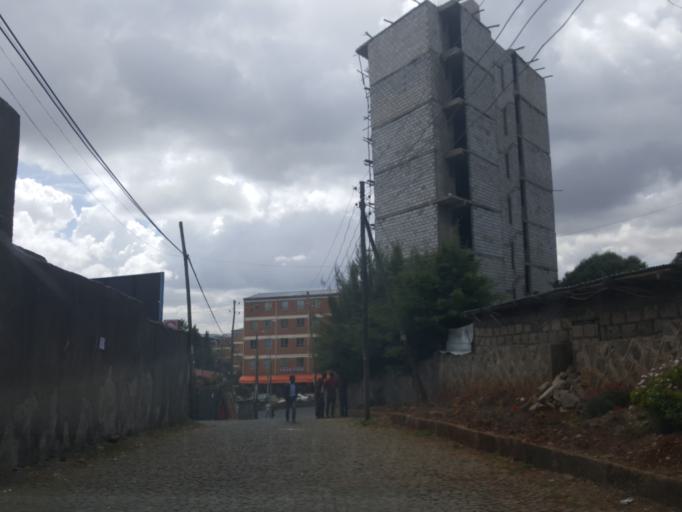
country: ET
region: Adis Abeba
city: Addis Ababa
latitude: 9.0646
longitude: 38.7338
